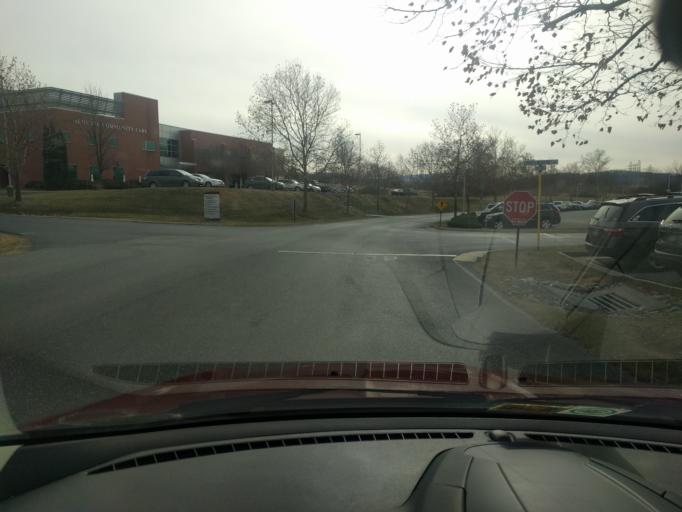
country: US
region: Virginia
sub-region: Augusta County
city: Fishersville
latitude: 38.0949
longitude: -78.9842
